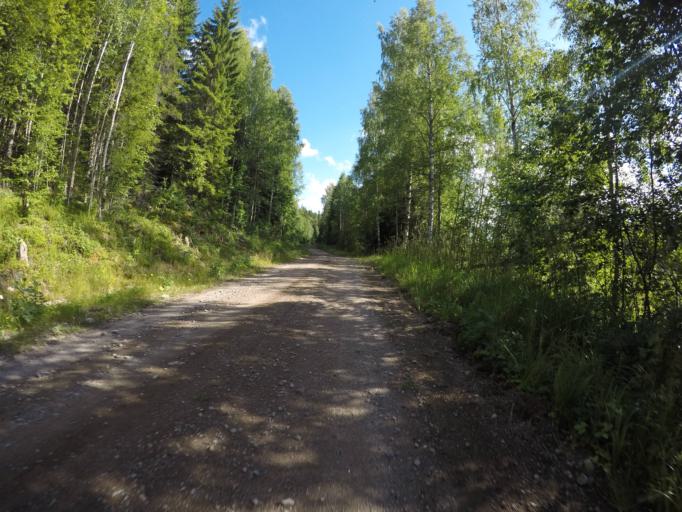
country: SE
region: OErebro
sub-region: Hallefors Kommun
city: Haellefors
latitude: 59.9930
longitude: 14.6062
